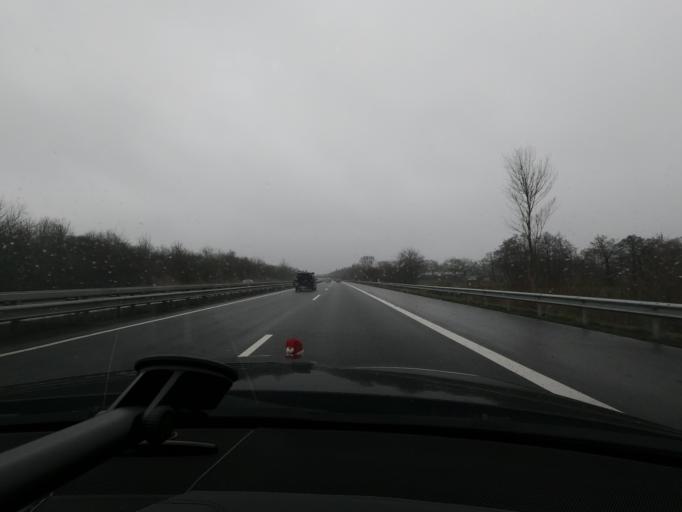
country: DE
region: Schleswig-Holstein
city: Bokel
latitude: 54.2406
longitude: 9.8210
